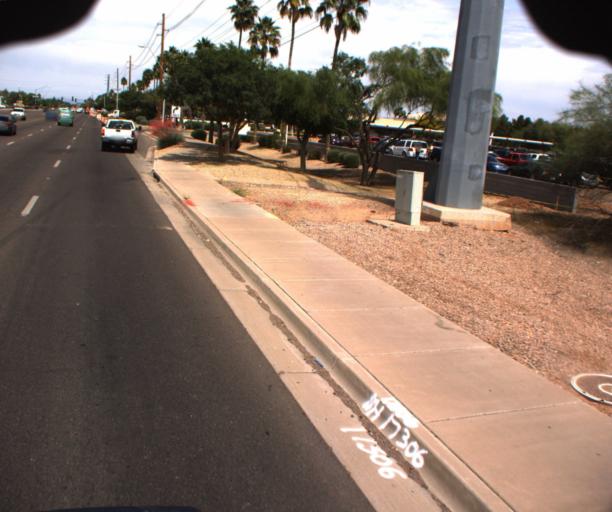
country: US
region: Arizona
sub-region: Maricopa County
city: San Carlos
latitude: 33.3612
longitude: -111.8417
